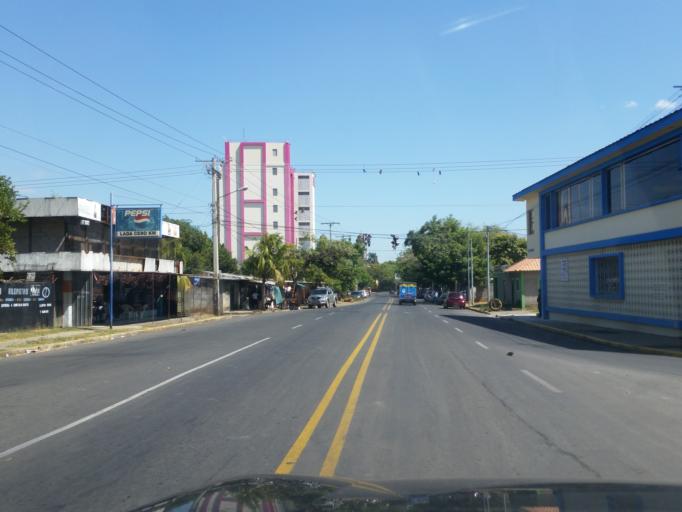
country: NI
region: Managua
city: Managua
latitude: 12.1569
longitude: -86.2765
